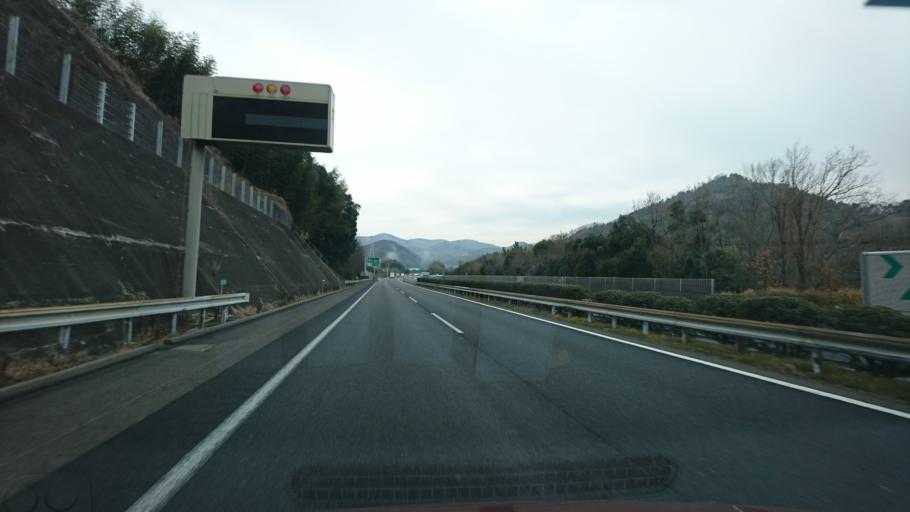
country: JP
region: Okayama
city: Kamogatacho-kamogata
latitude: 34.5525
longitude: 133.5979
